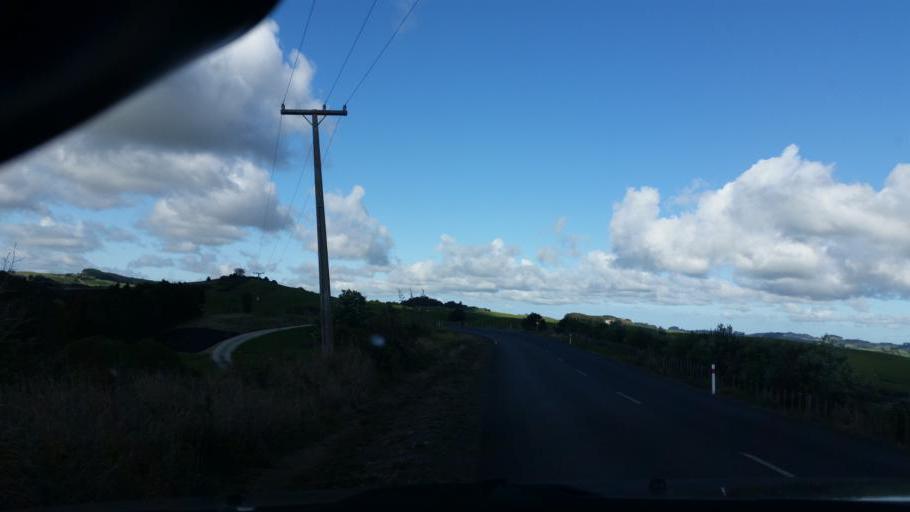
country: NZ
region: Auckland
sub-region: Auckland
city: Wellsford
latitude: -36.1507
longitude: 174.5435
